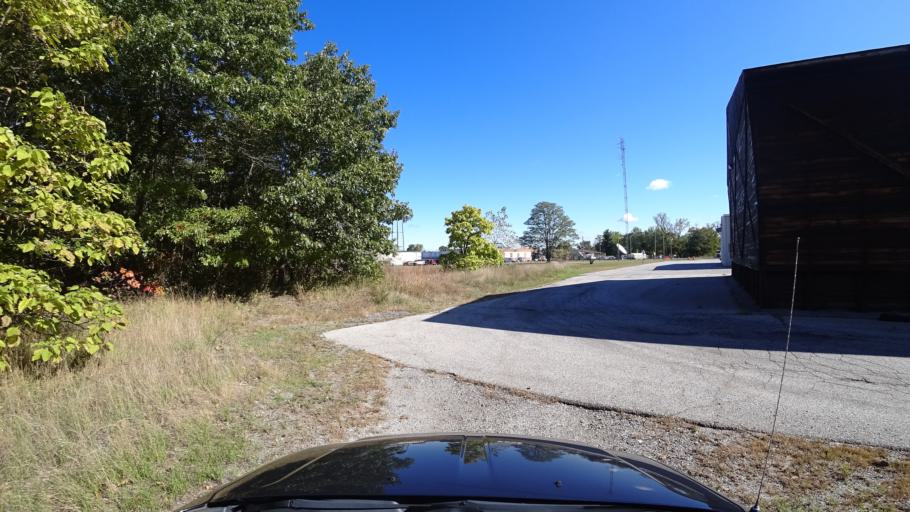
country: US
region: Indiana
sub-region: LaPorte County
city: Michigan City
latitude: 41.7015
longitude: -86.9105
